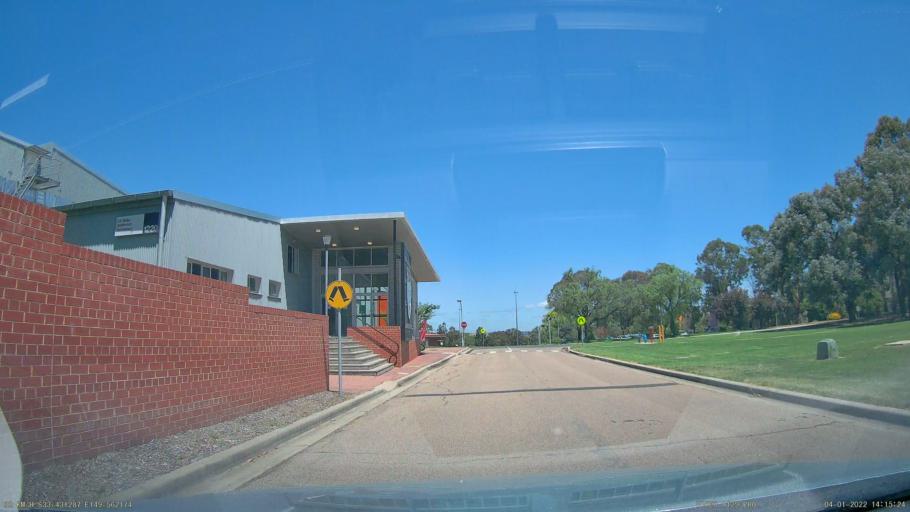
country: AU
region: New South Wales
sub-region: Bathurst Regional
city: Bathurst
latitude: -33.4314
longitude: 149.5622
